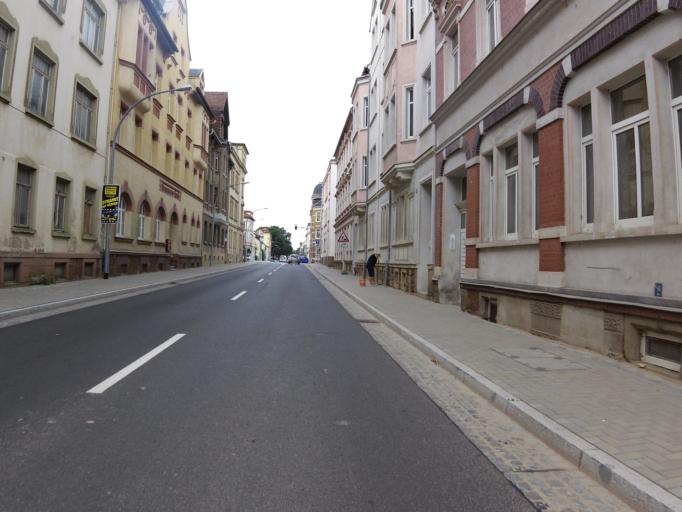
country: DE
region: Saxony
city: Dobeln
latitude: 51.1198
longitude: 13.1161
